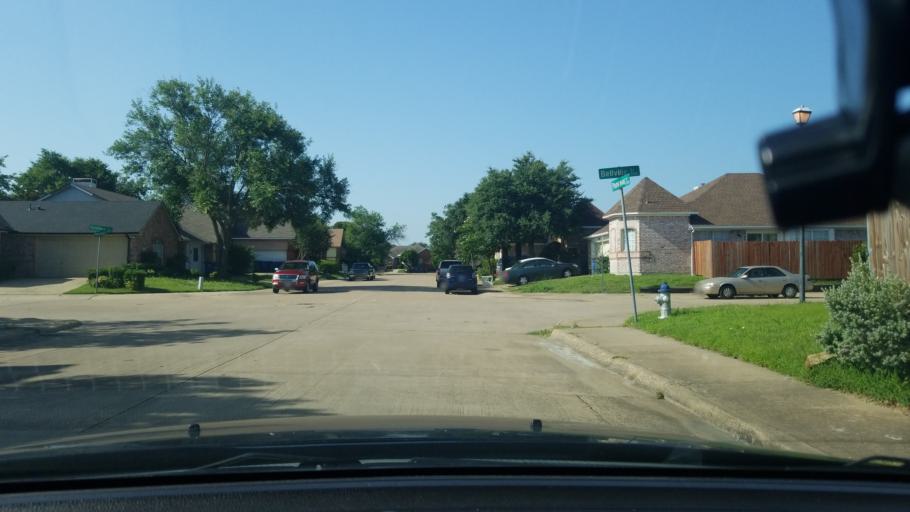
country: US
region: Texas
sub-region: Dallas County
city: Mesquite
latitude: 32.8069
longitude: -96.6787
